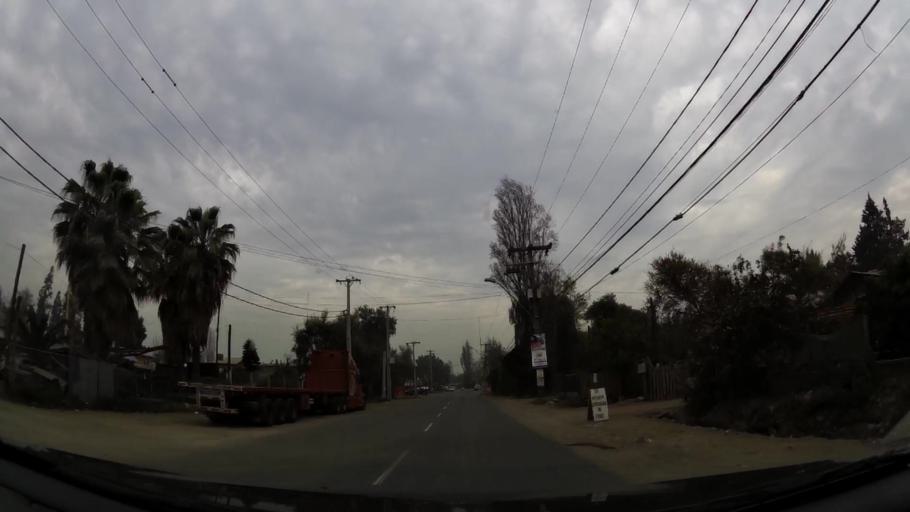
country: CL
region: Santiago Metropolitan
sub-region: Provincia de Chacabuco
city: Chicureo Abajo
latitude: -33.2721
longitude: -70.7450
